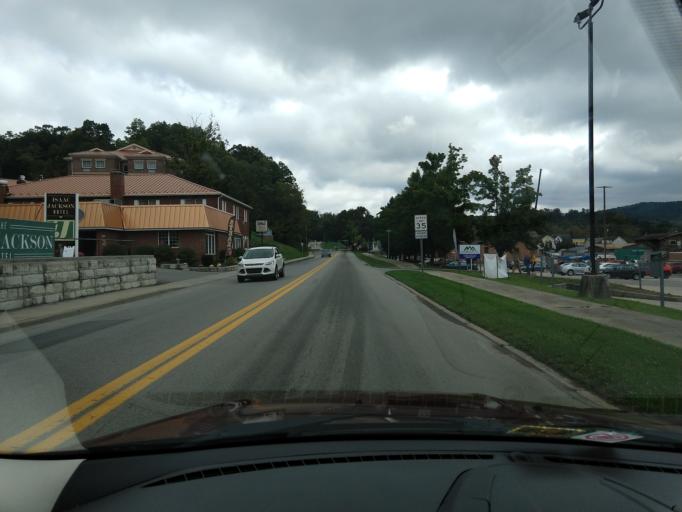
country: US
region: West Virginia
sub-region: Randolph County
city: Elkins
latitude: 38.9287
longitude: -79.8551
